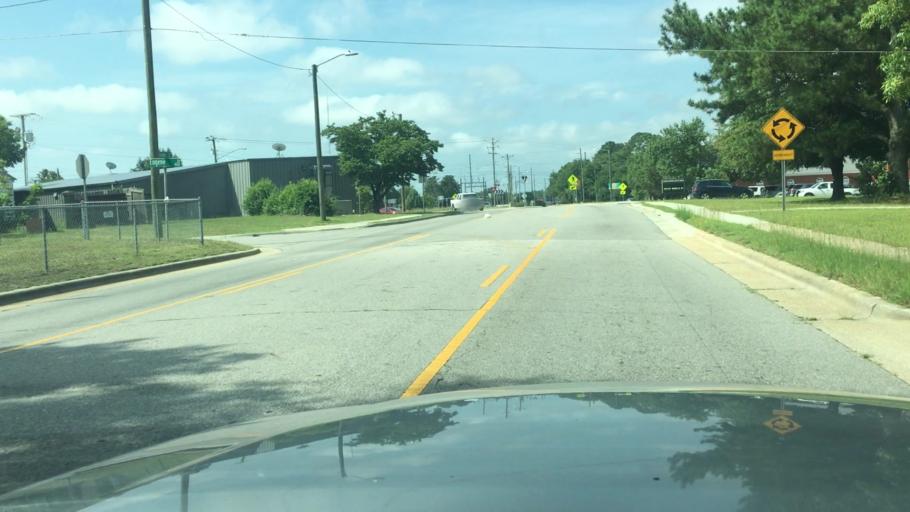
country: US
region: North Carolina
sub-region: Cumberland County
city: Fayetteville
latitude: 35.0234
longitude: -78.9013
